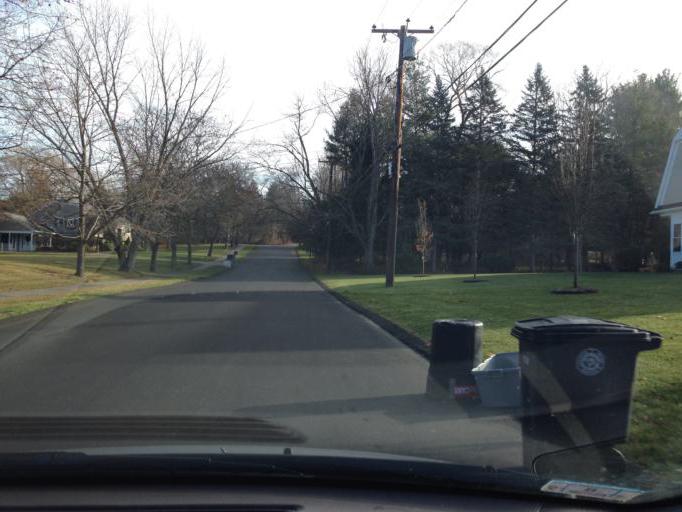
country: US
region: Massachusetts
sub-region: Middlesex County
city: Bedford
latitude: 42.5036
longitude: -71.2867
